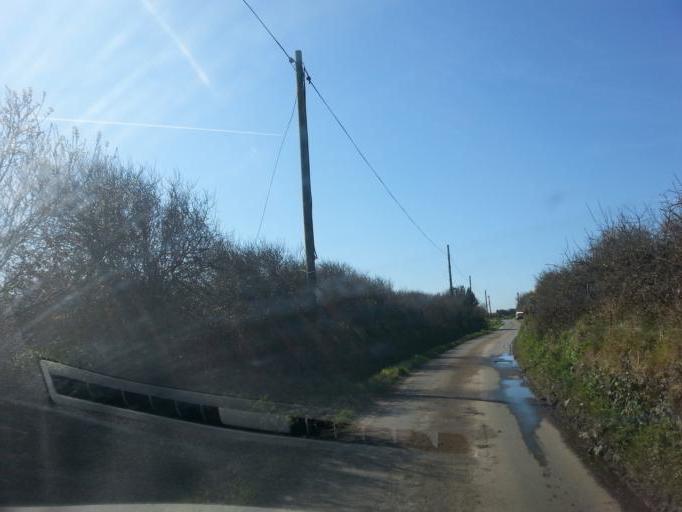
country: GB
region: England
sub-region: Cornwall
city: Landewednack
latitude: 49.9862
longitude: -5.1949
